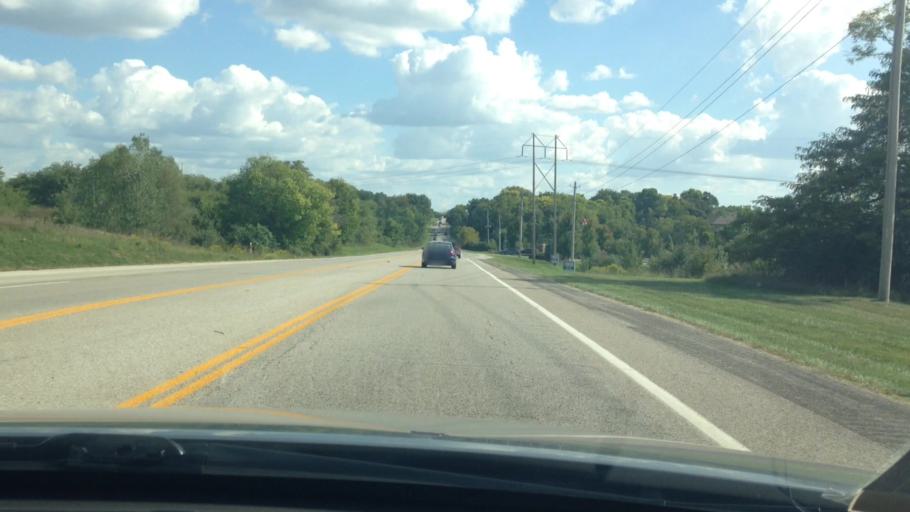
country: US
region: Missouri
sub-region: Clay County
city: Liberty
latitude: 39.2783
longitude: -94.4659
